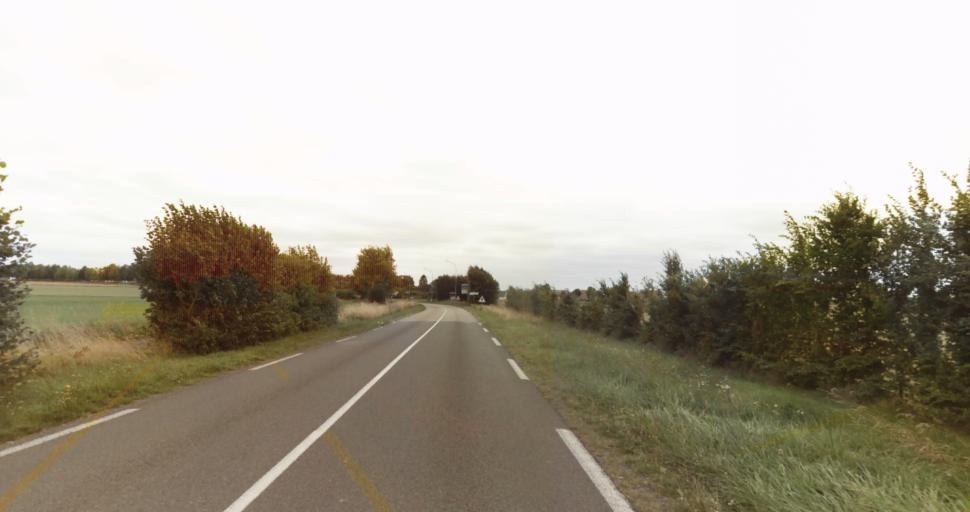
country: FR
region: Haute-Normandie
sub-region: Departement de l'Eure
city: Marcilly-sur-Eure
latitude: 48.9148
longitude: 1.2791
